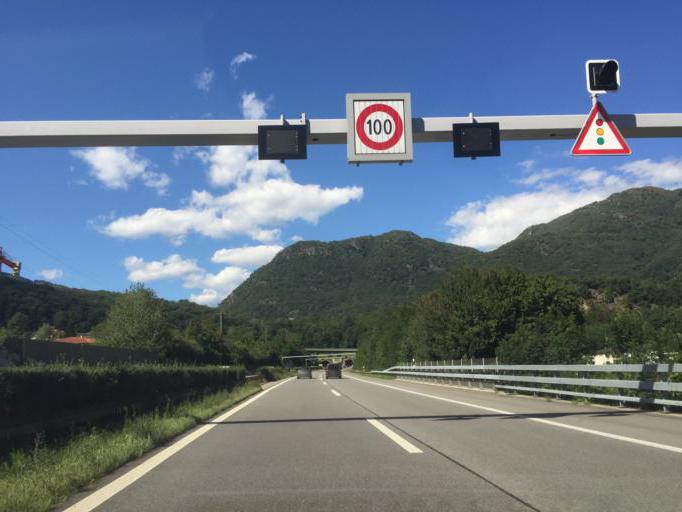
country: CH
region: Ticino
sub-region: Lugano District
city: Gravesano
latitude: 46.0635
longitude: 8.9279
